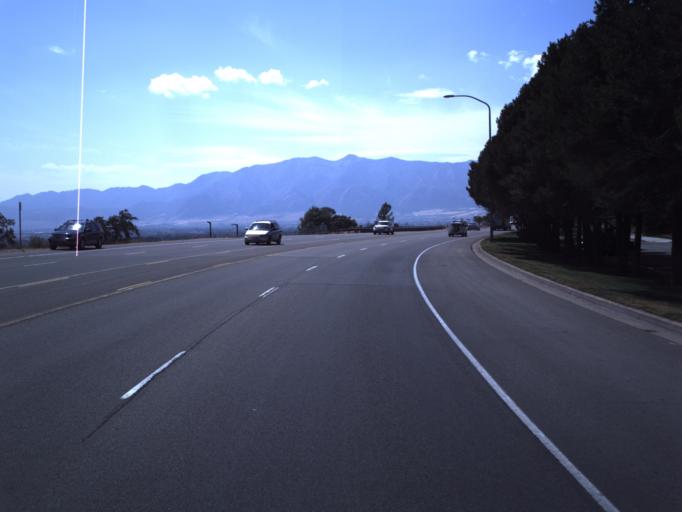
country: US
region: Utah
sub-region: Cache County
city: River Heights
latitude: 41.7412
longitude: -111.8067
